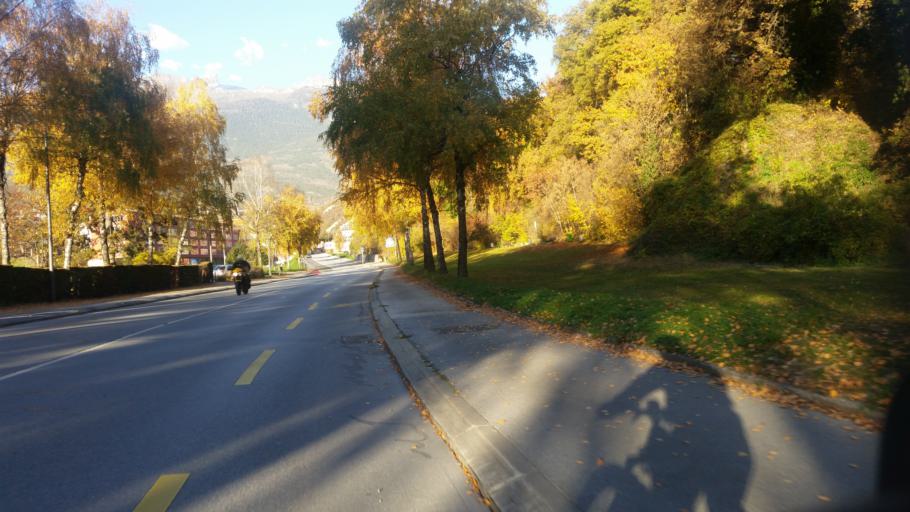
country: CH
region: Valais
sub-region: Sierre District
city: Sierre
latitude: 46.2901
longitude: 7.5352
